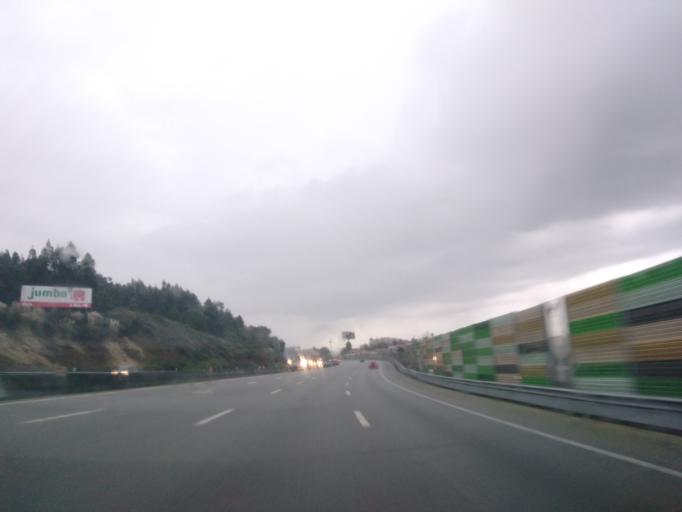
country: PT
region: Porto
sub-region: Maia
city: Milheiros
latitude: 41.2212
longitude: -8.5744
